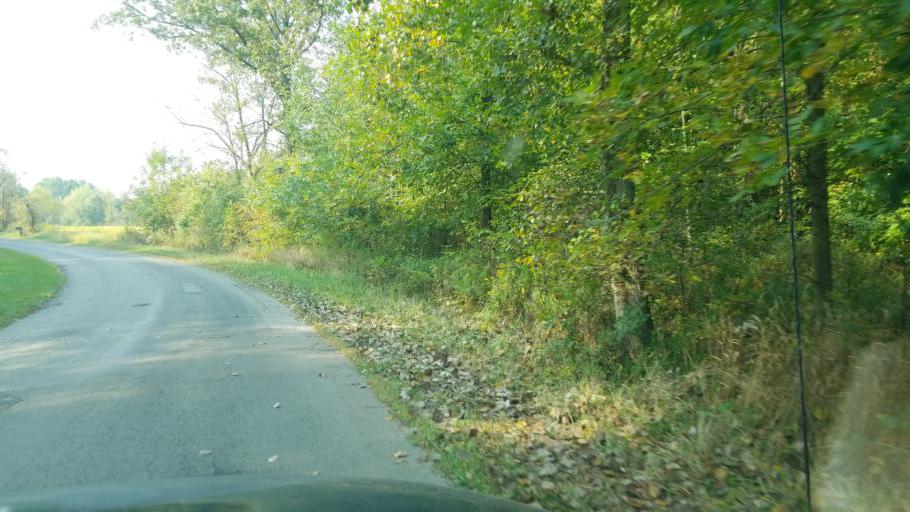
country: US
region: Ohio
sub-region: Licking County
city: Utica
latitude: 40.2526
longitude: -82.5756
